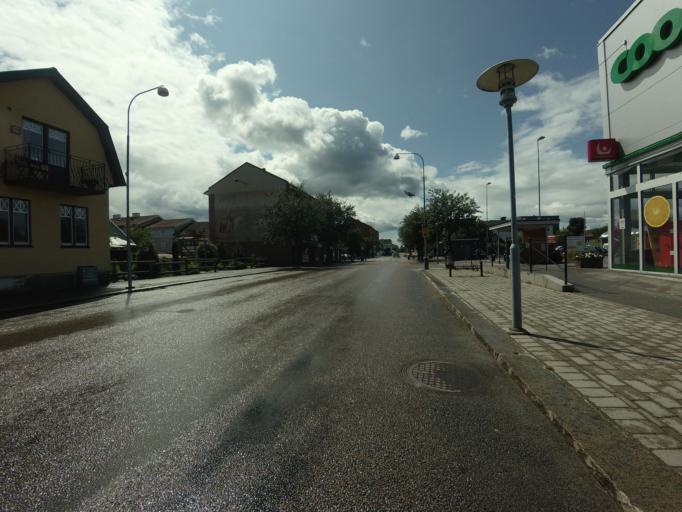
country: SE
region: Skane
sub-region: Osby Kommun
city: Osby
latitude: 56.3831
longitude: 13.9950
